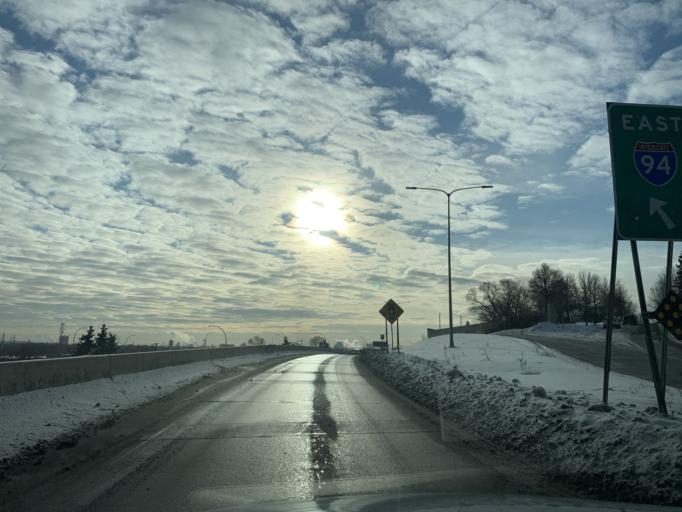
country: US
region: Minnesota
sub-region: Anoka County
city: Columbia Heights
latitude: 45.0232
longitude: -93.2851
